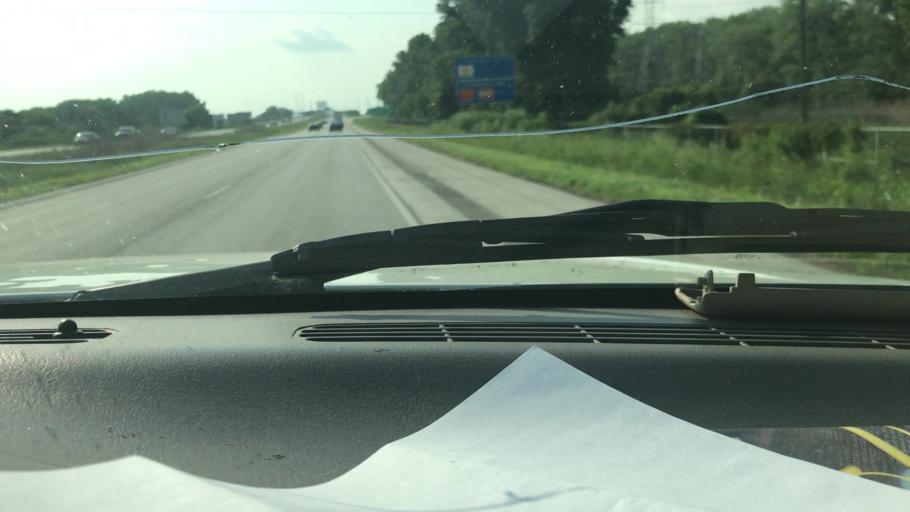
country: US
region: Wisconsin
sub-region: Brown County
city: Green Bay
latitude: 44.5232
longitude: -87.9773
